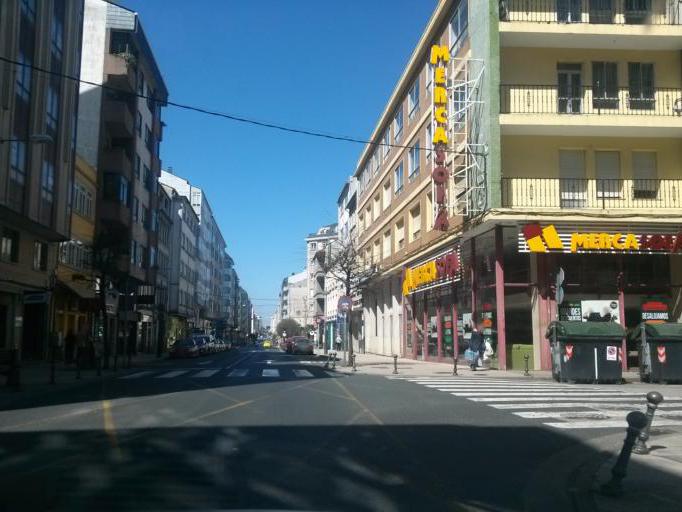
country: ES
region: Galicia
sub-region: Provincia de Lugo
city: Lugo
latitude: 43.0187
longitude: -7.5617
